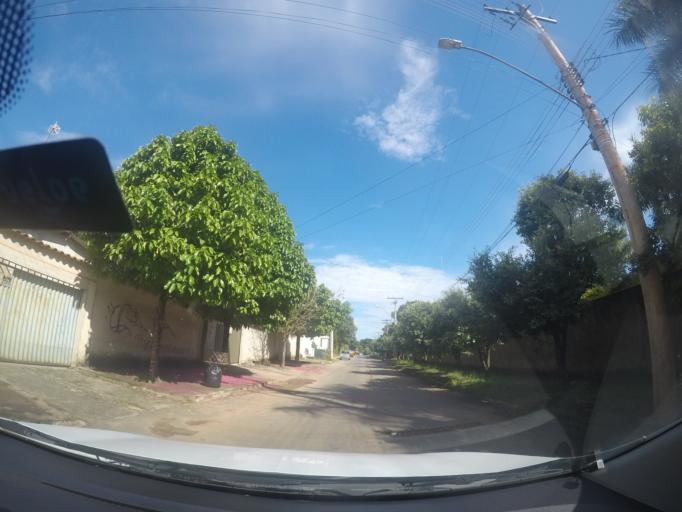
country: BR
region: Goias
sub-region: Goiania
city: Goiania
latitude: -16.6598
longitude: -49.2063
